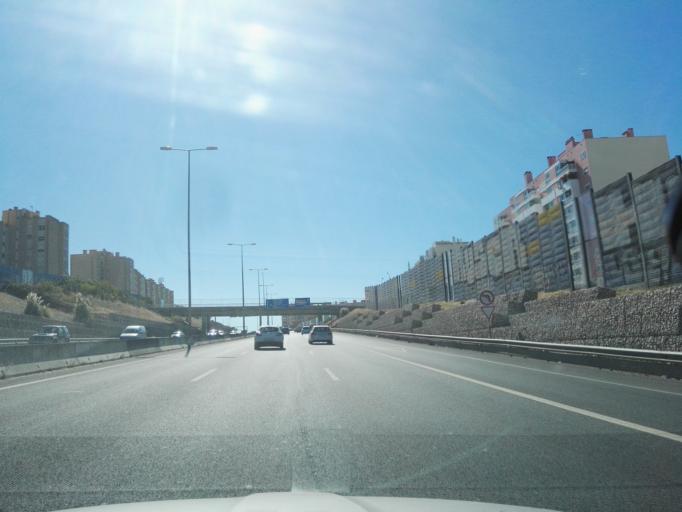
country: PT
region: Lisbon
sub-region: Odivelas
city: Olival do Basto
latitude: 38.7702
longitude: -9.1672
